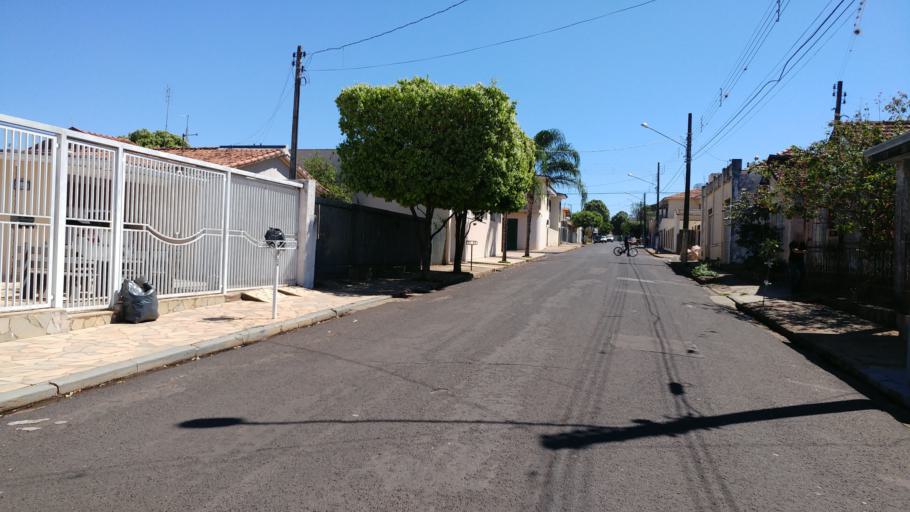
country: BR
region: Sao Paulo
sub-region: Paraguacu Paulista
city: Paraguacu Paulista
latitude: -22.4172
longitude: -50.5765
